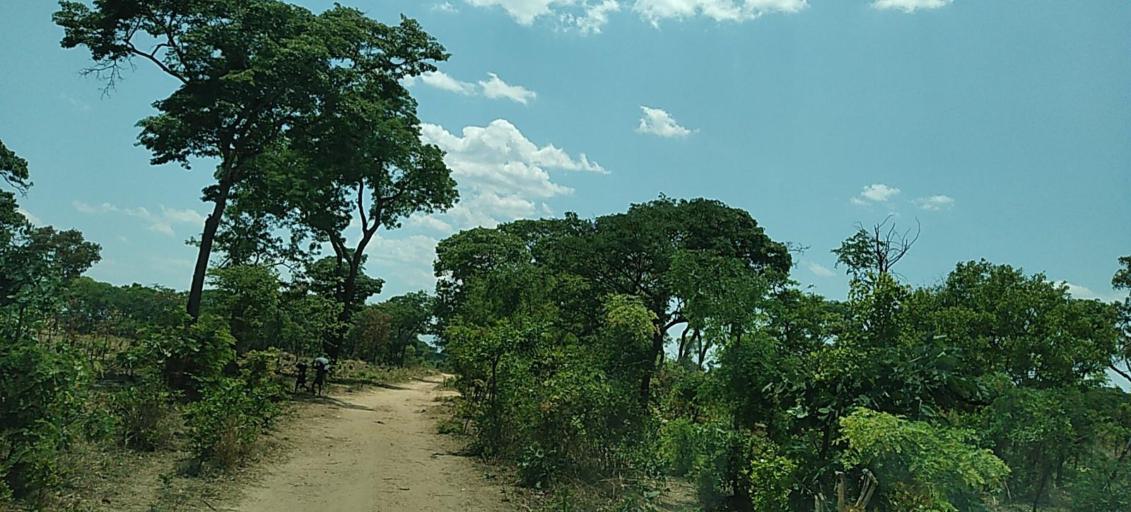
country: ZM
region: Central
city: Kapiri Mposhi
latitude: -13.6333
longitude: 28.7567
